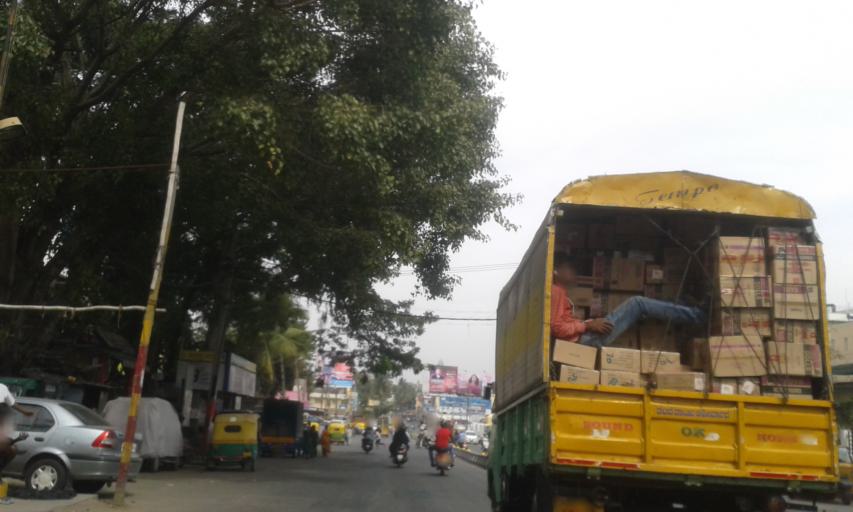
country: IN
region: Karnataka
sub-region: Bangalore Urban
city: Bangalore
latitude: 12.9400
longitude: 77.6022
